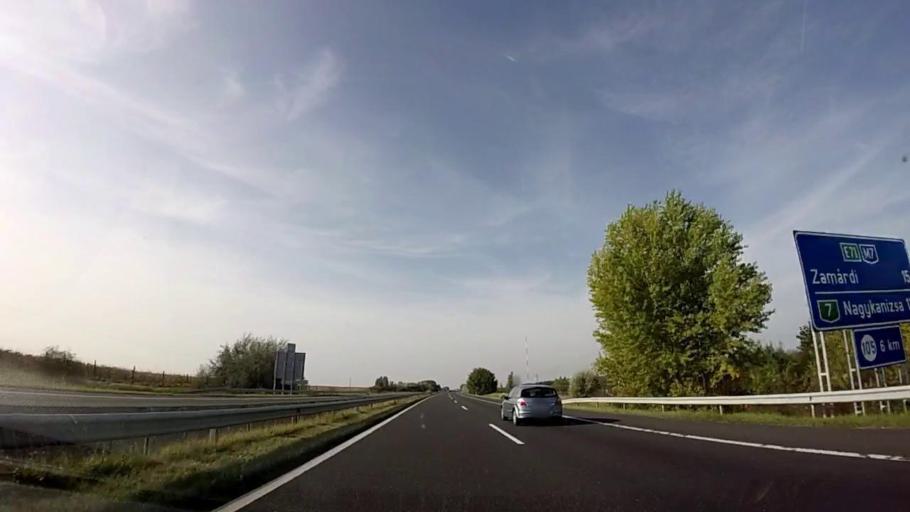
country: HU
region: Somogy
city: Balatonszabadi
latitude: 46.9250
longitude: 18.1278
